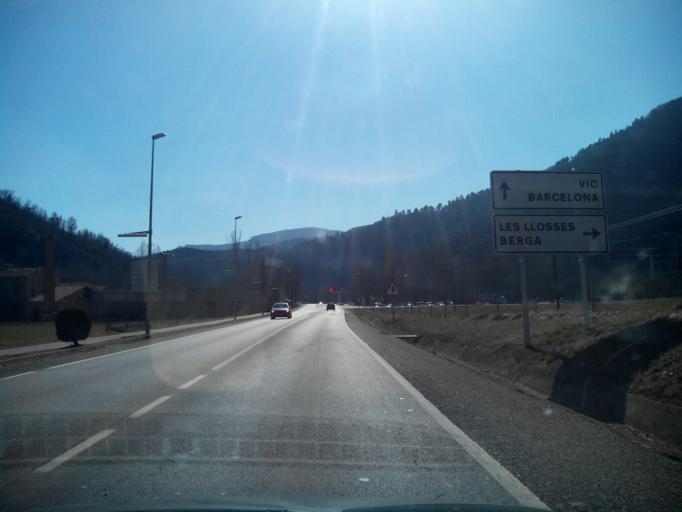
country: ES
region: Catalonia
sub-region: Provincia de Girona
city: Ripoll
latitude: 42.1802
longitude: 2.1947
